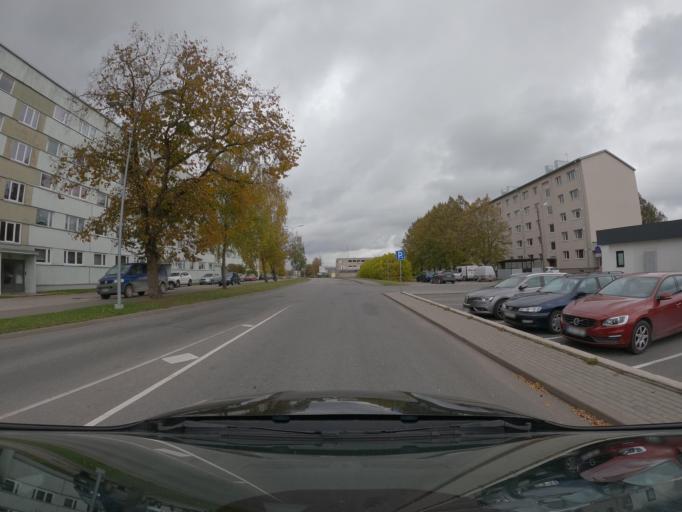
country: EE
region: Saare
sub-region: Kuressaare linn
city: Kuressaare
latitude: 58.2625
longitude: 22.4842
